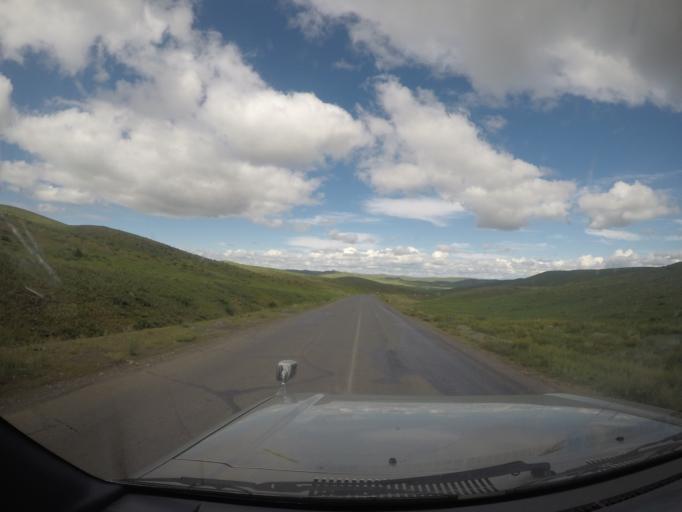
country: MN
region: Hentiy
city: Bayanbulag
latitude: 47.4442
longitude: 109.7680
